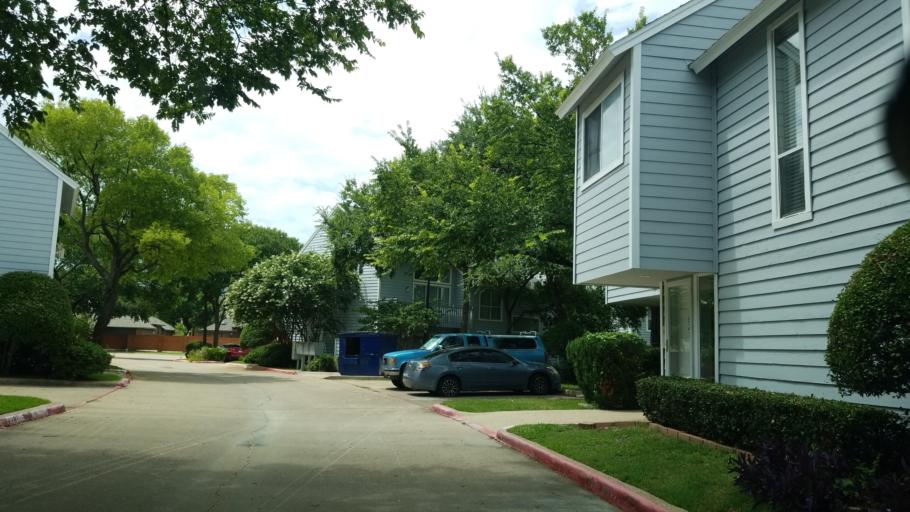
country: US
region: Texas
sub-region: Dallas County
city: Farmers Branch
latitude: 32.9337
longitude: -96.9547
